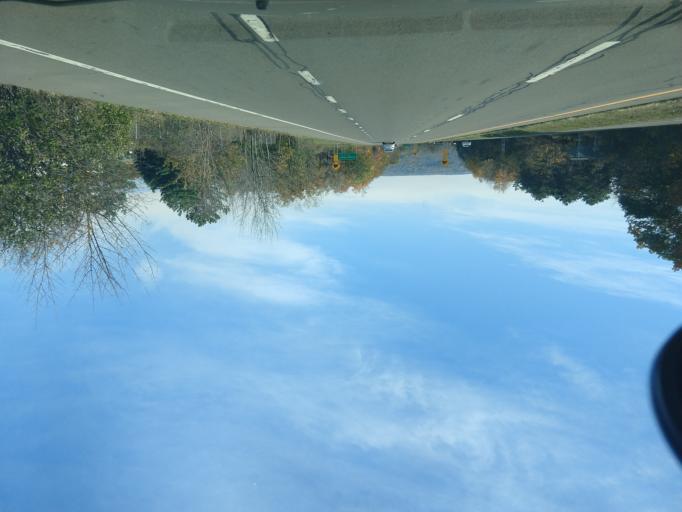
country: US
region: New York
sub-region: Tompkins County
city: Lansing
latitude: 42.4809
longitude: -76.4885
